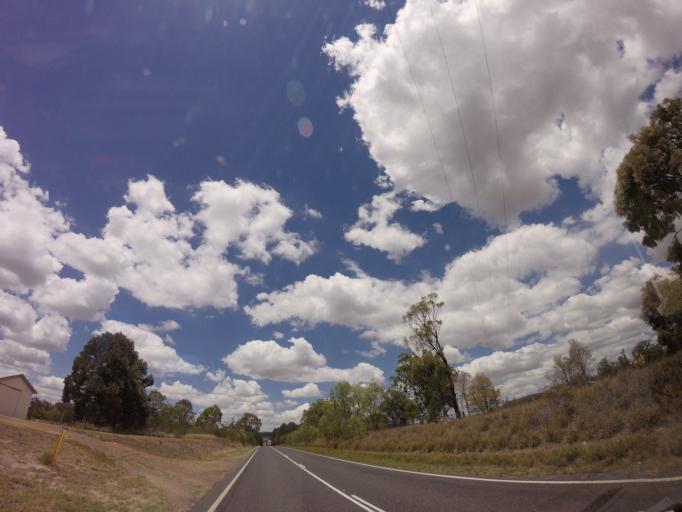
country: AU
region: Queensland
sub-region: Toowoomba
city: Oakey
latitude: -27.9413
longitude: 151.1571
